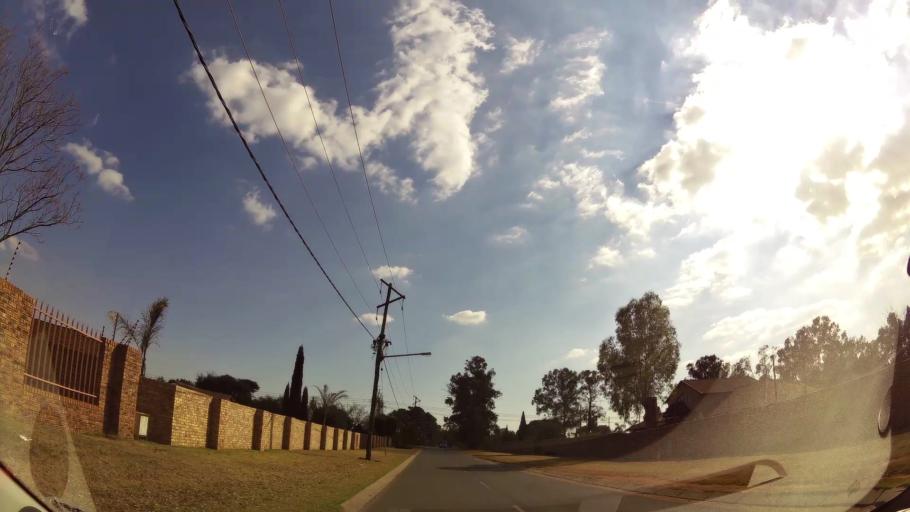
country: ZA
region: Gauteng
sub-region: Ekurhuleni Metropolitan Municipality
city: Benoni
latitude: -26.1131
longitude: 28.3431
